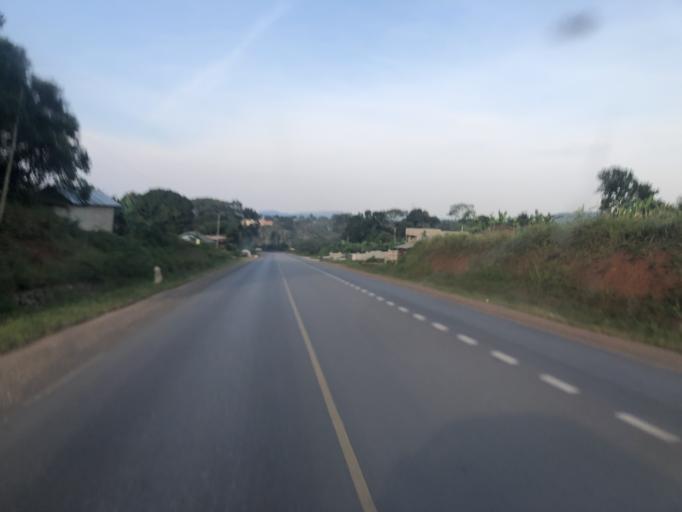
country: UG
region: Central Region
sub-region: Mpigi District
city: Mpigi
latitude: 0.2028
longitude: 32.3039
